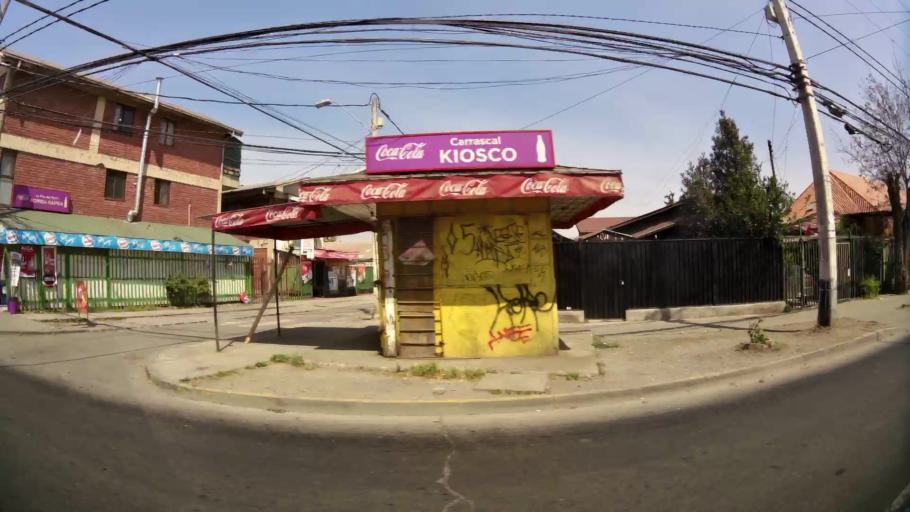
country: CL
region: Santiago Metropolitan
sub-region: Provincia de Santiago
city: Lo Prado
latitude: -33.4164
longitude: -70.7124
